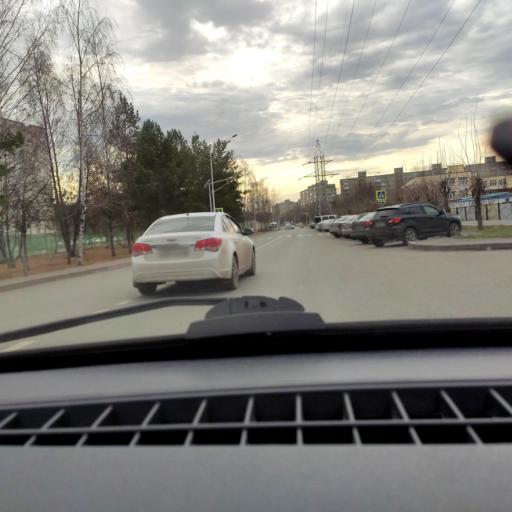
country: RU
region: Bashkortostan
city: Ufa
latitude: 54.7044
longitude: 56.0074
